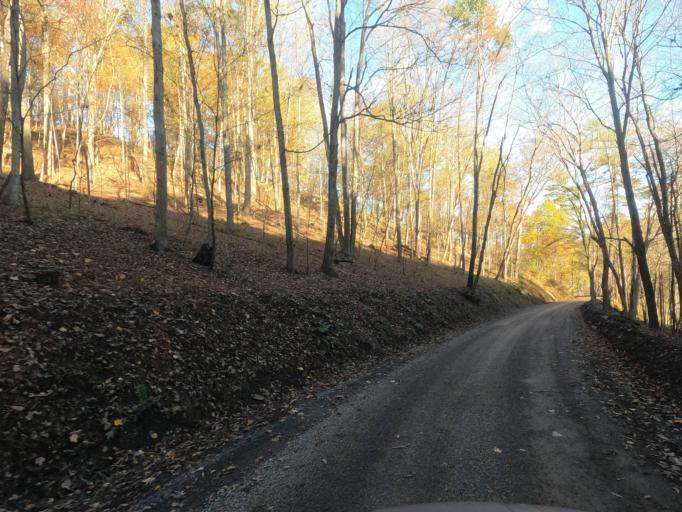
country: US
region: West Virginia
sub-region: Morgan County
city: Berkeley Springs
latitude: 39.6582
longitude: -78.4586
